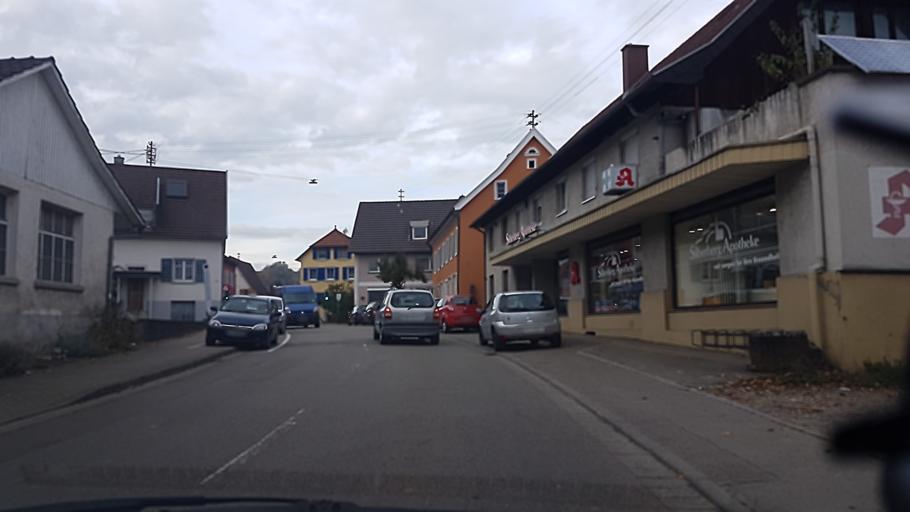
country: DE
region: Baden-Wuerttemberg
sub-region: Freiburg Region
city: Bahlingen
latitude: 48.1204
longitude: 7.7401
